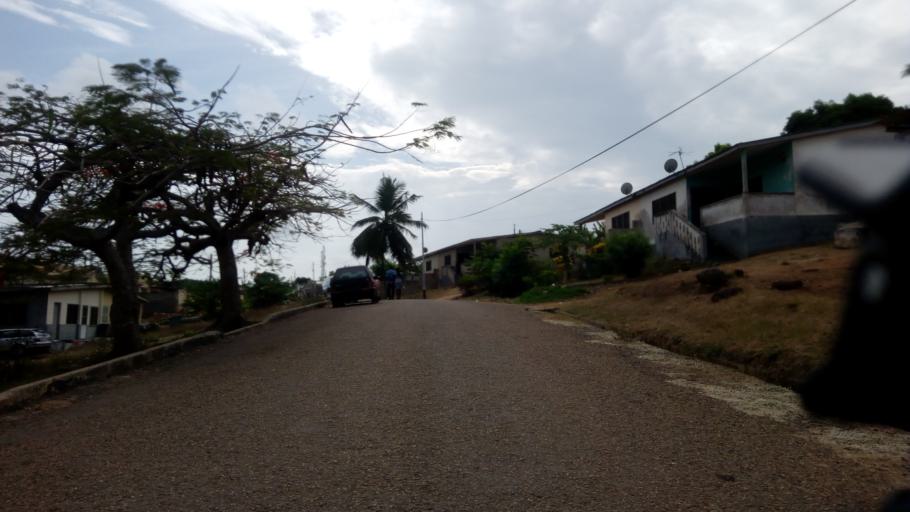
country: GH
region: Central
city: Cape Coast
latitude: 5.1052
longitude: -1.2781
